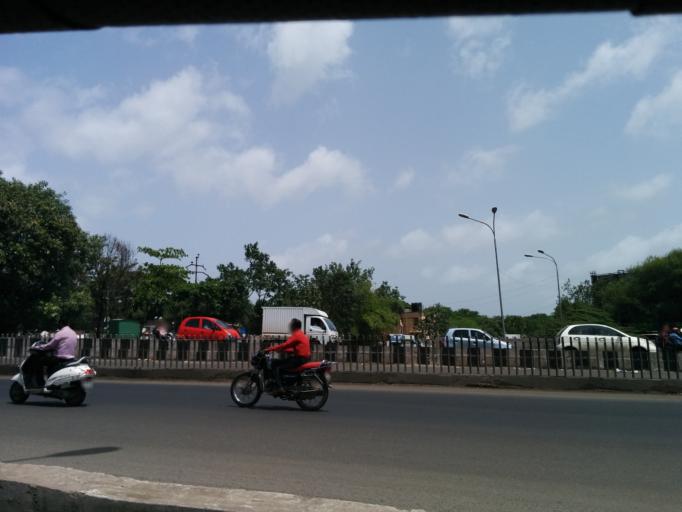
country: IN
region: Maharashtra
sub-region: Pune Division
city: Lohogaon
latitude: 18.5556
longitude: 73.9070
